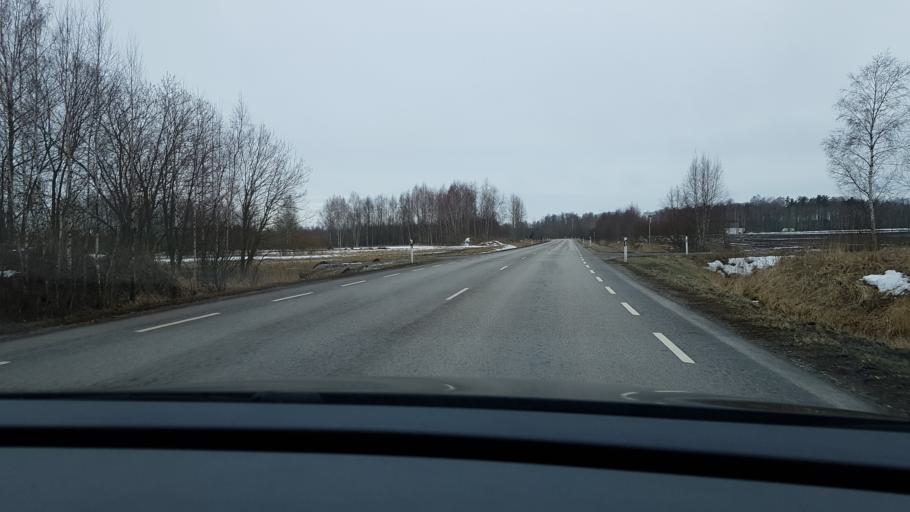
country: EE
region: Paernumaa
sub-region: Sauga vald
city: Sauga
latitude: 58.4085
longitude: 24.4369
